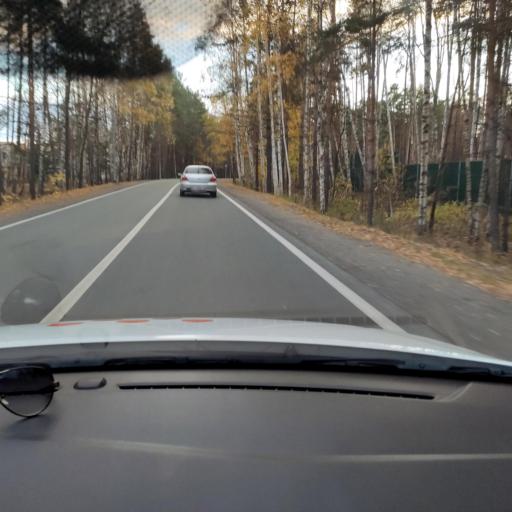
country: RU
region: Tatarstan
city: Verkhniy Uslon
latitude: 55.6339
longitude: 49.0187
